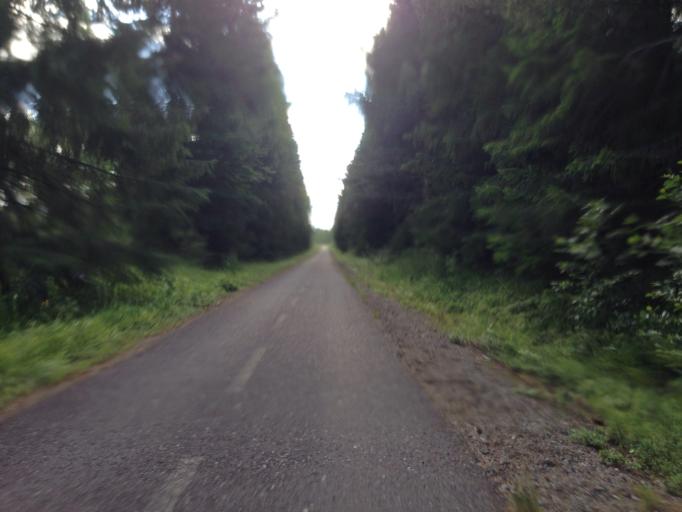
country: SE
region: Dalarna
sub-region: Ludvika Kommun
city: Ludvika
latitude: 60.2025
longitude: 15.1010
